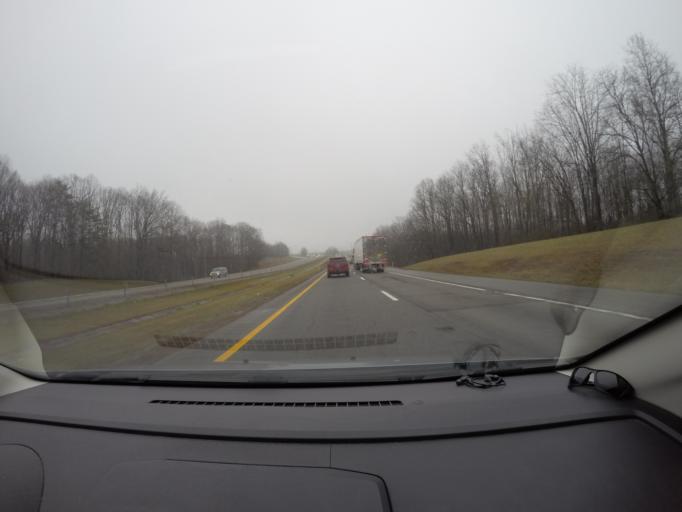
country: US
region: Tennessee
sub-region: Marion County
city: Monteagle
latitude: 35.2338
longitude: -85.8336
